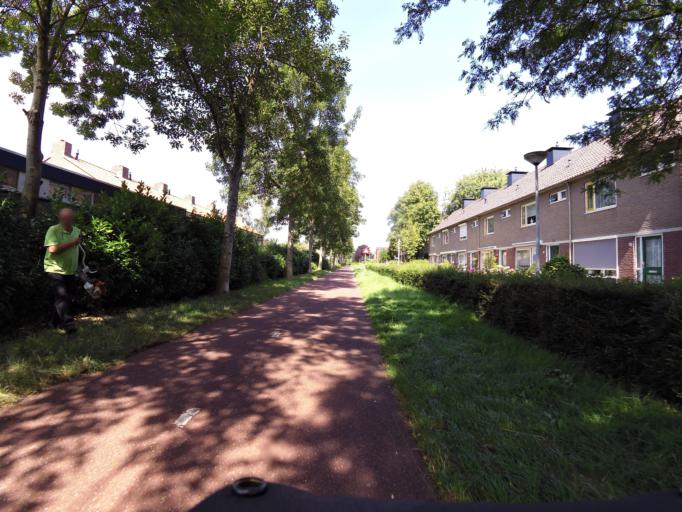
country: NL
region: South Holland
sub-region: Gemeente Barendrecht
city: Barendrecht
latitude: 51.8563
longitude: 4.5290
